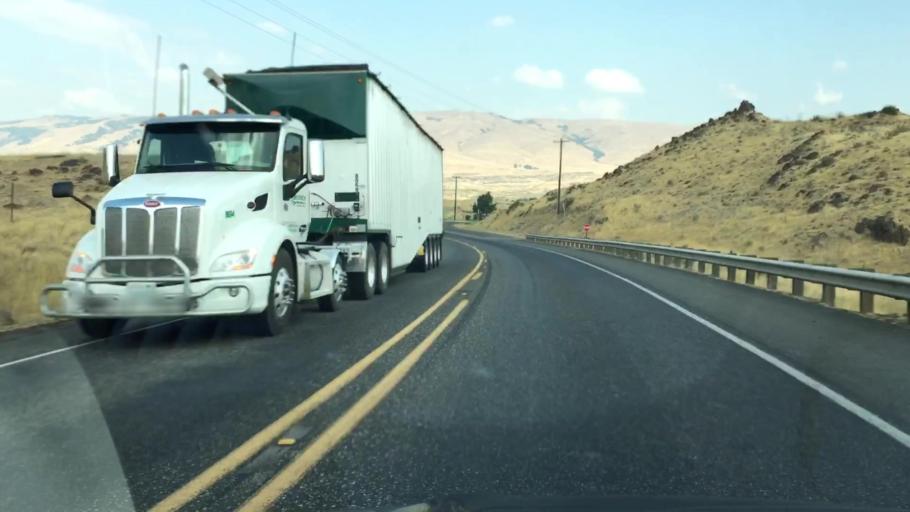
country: US
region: Washington
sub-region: Klickitat County
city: Dallesport
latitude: 45.6192
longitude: -121.1461
